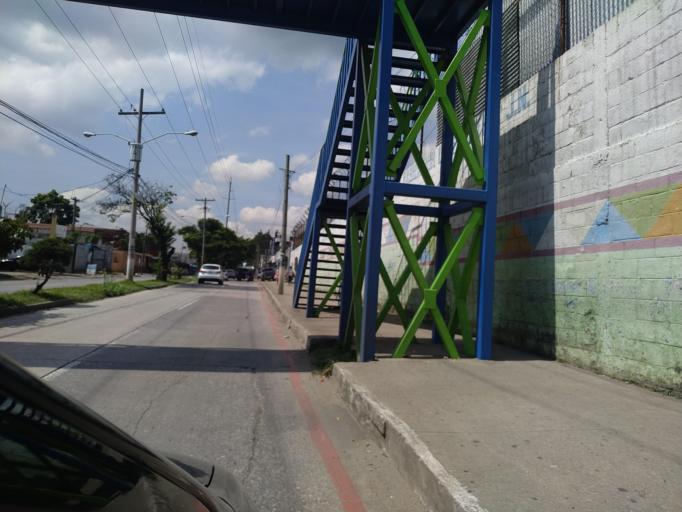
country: GT
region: Guatemala
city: Mixco
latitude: 14.6685
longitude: -90.5834
